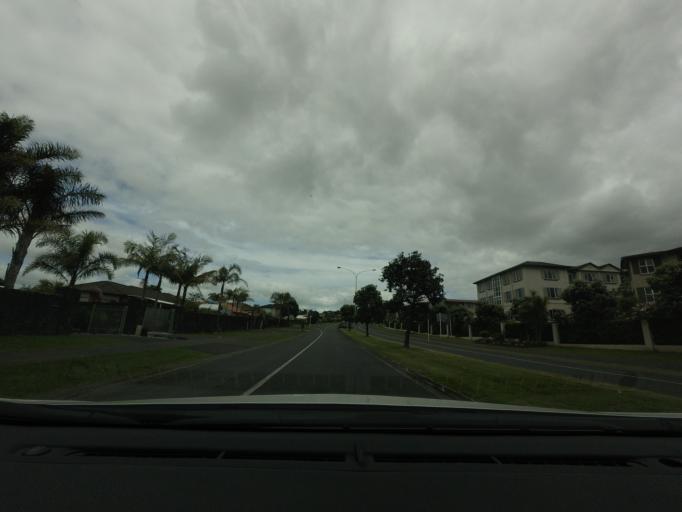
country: NZ
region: Auckland
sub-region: Auckland
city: Rothesay Bay
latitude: -36.5850
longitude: 174.6855
